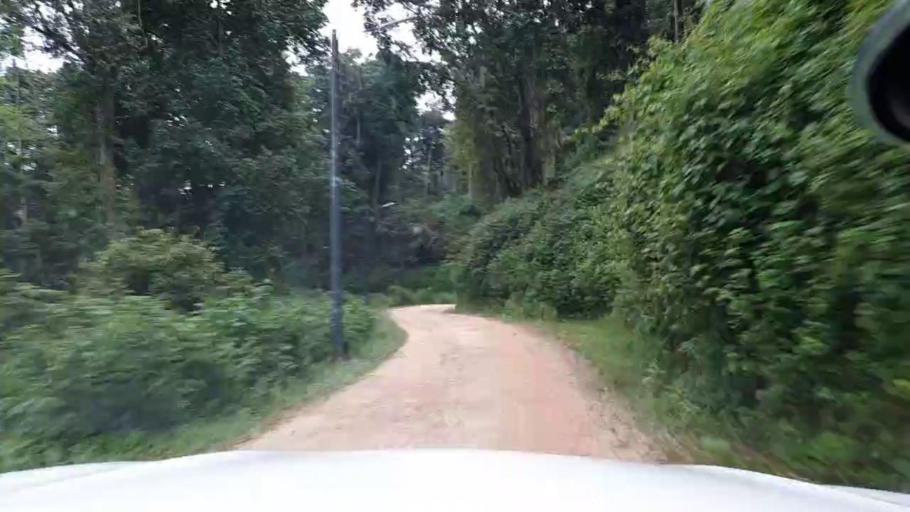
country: RW
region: Western Province
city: Cyangugu
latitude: -2.5594
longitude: 29.2287
